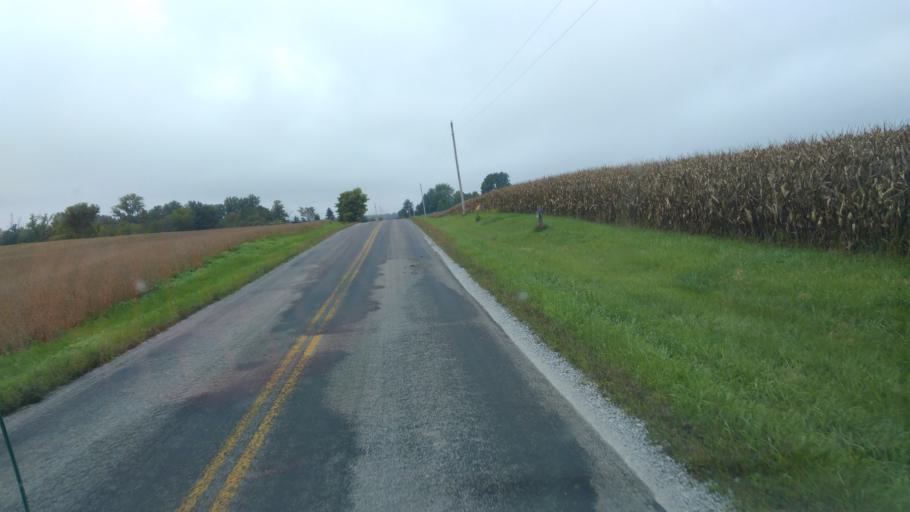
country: US
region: Ohio
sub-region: Hardin County
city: Kenton
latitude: 40.5564
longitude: -83.6359
